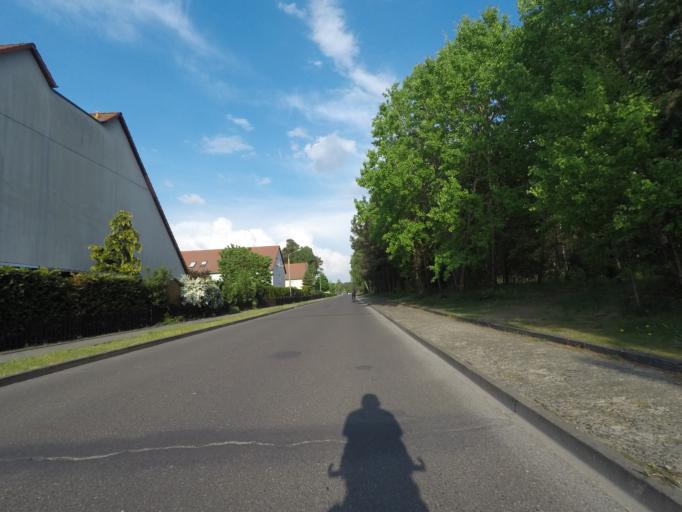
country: DE
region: Brandenburg
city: Eberswalde
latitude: 52.8280
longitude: 13.7600
